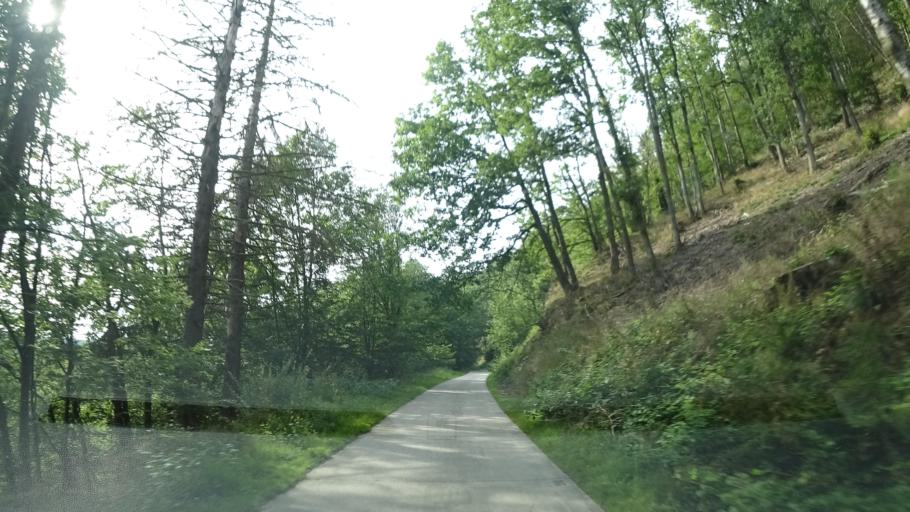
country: BE
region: Wallonia
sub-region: Province du Luxembourg
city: Herbeumont
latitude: 49.7722
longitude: 5.2482
